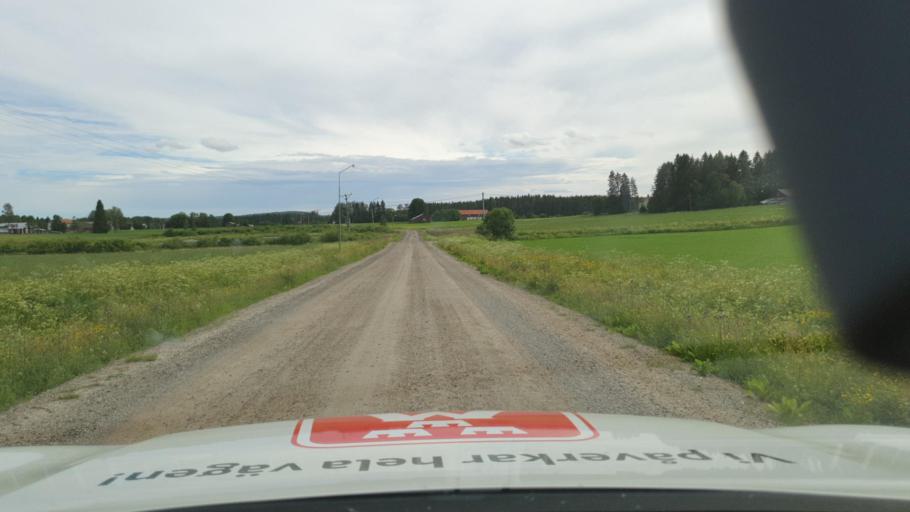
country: SE
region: Vaesterbotten
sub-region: Skelleftea Kommun
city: Burea
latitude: 64.3652
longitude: 21.0861
